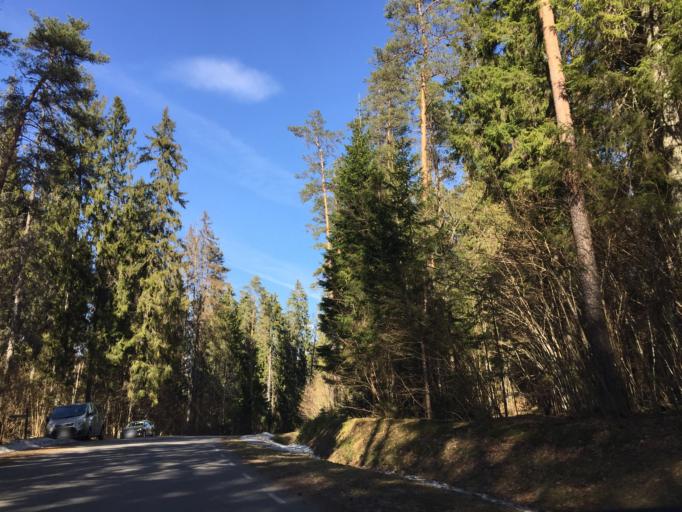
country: EE
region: Vorumaa
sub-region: Antsla vald
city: Vana-Antsla
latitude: 58.0296
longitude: 26.4745
